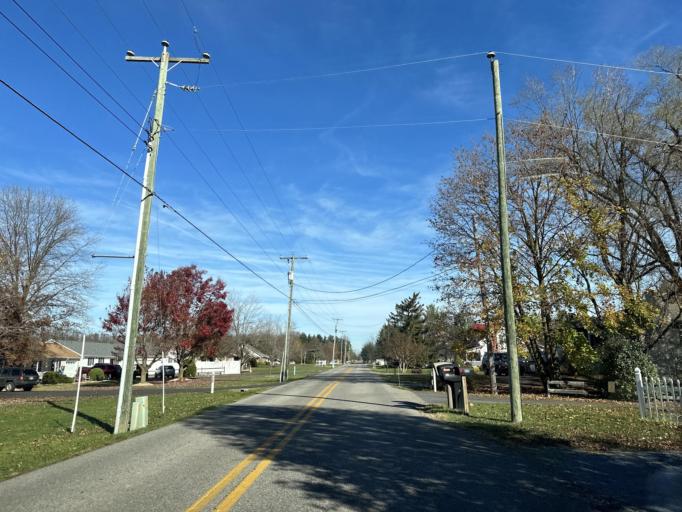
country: US
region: Virginia
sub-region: Augusta County
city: Crimora
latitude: 38.2061
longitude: -78.9034
